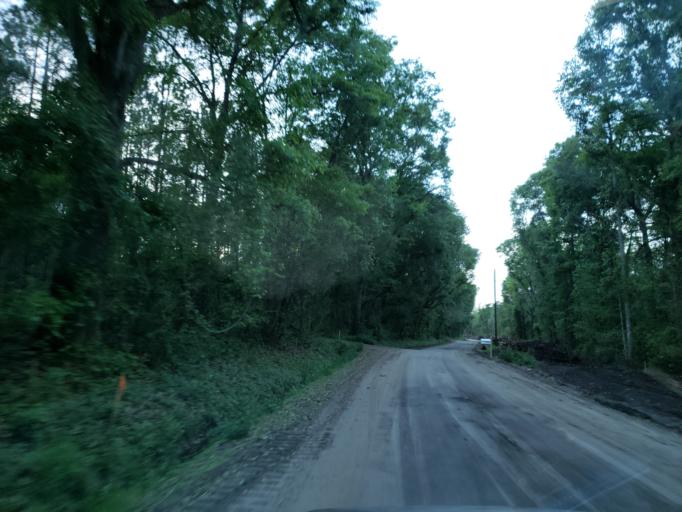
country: US
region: Georgia
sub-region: Lowndes County
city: Hahira
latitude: 30.9521
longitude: -83.3901
